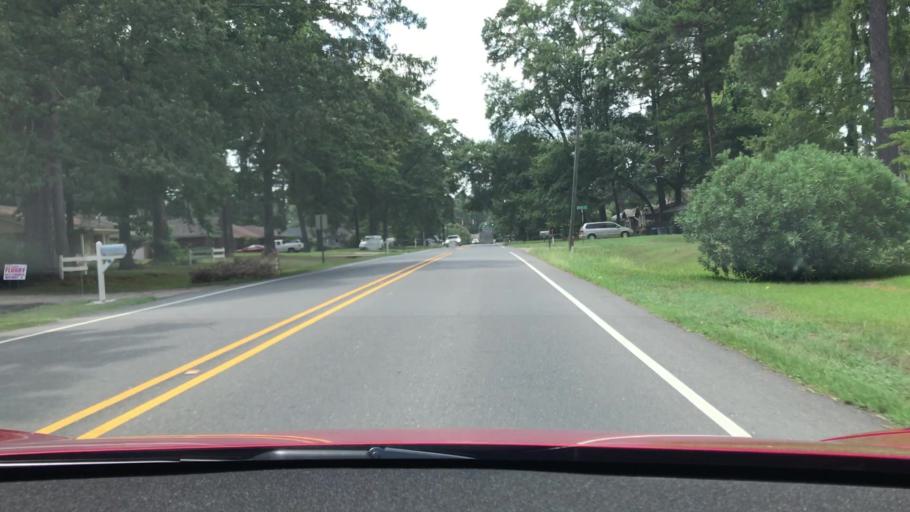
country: US
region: Louisiana
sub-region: De Soto Parish
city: Stonewall
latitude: 32.3904
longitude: -93.7940
